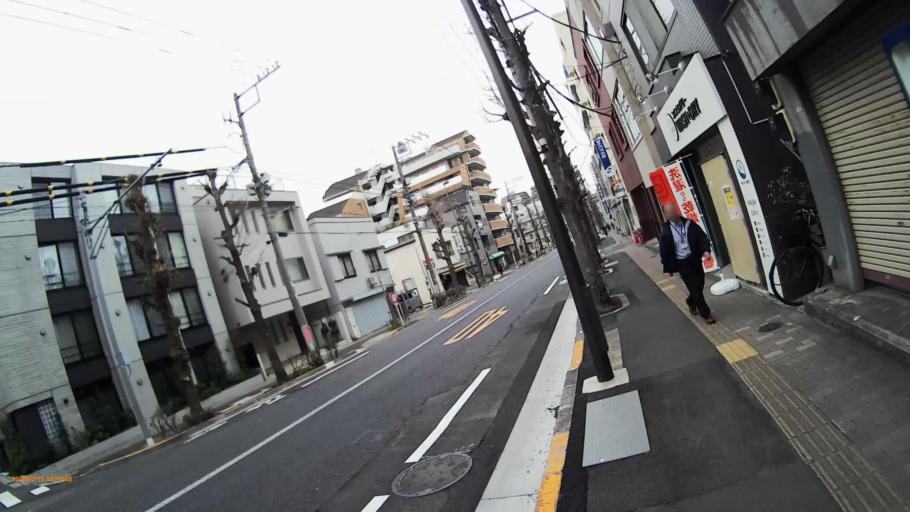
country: JP
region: Tokyo
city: Tokyo
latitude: 35.7253
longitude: 139.7495
